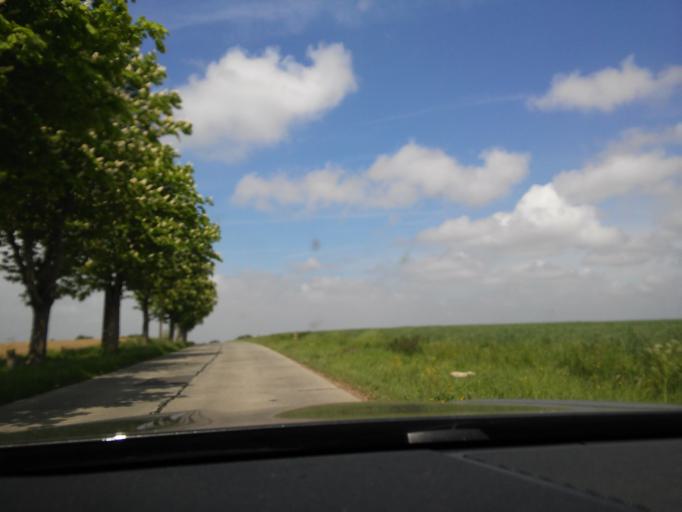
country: BE
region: Wallonia
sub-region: Province du Brabant Wallon
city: Tubize
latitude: 50.7191
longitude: 4.1793
